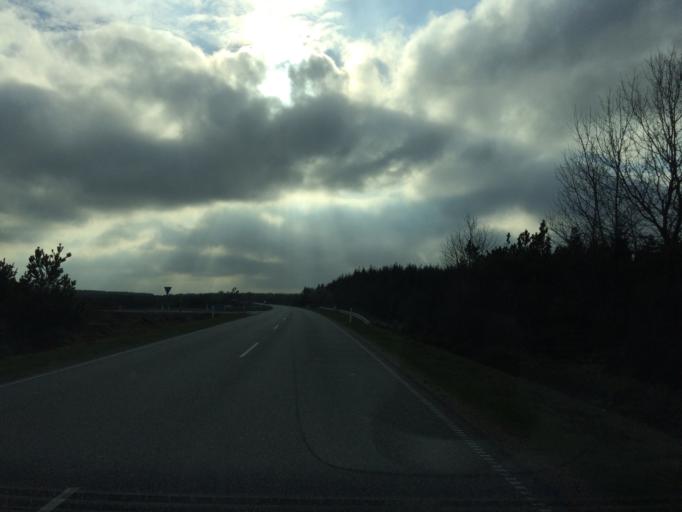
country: DK
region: Central Jutland
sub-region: Viborg Kommune
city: Karup
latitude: 56.3402
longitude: 9.0714
